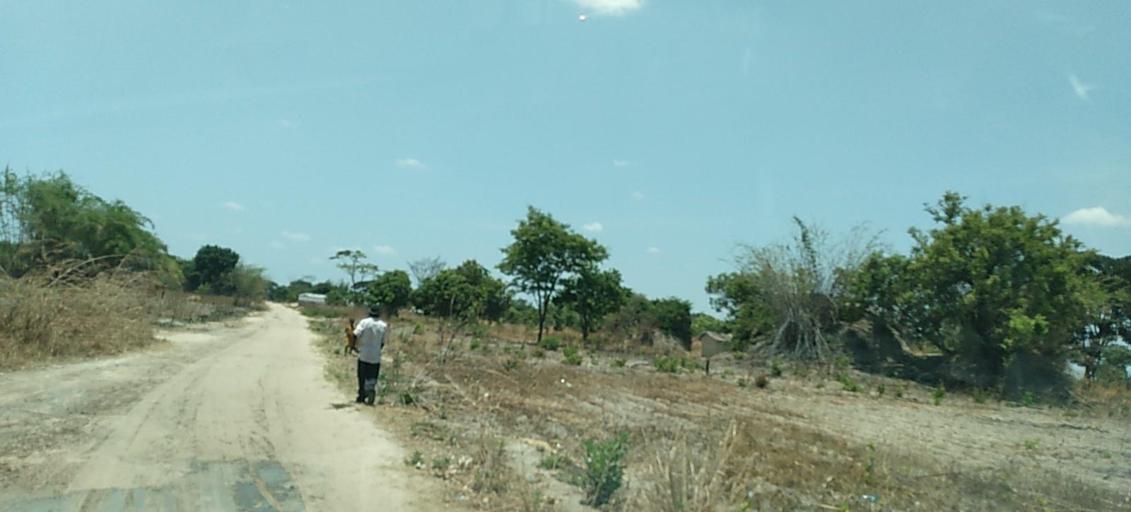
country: ZM
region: Copperbelt
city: Luanshya
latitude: -13.0751
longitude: 28.4049
